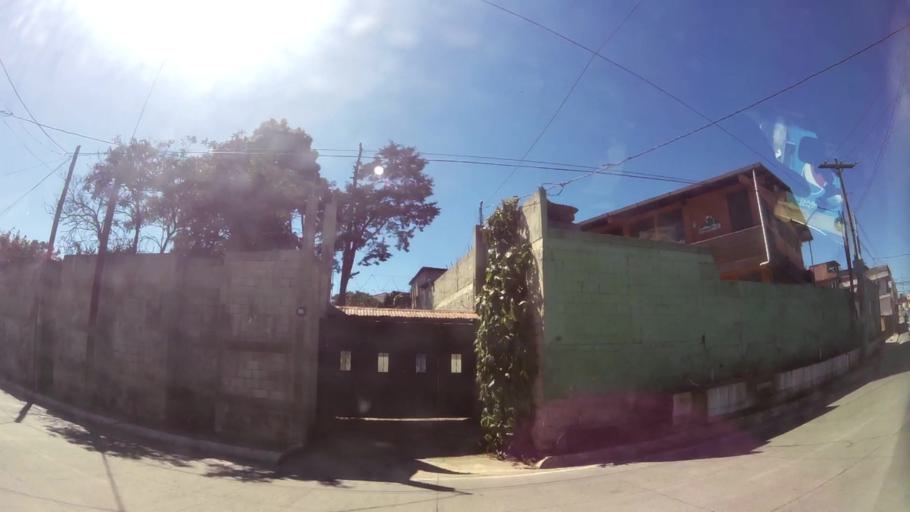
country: GT
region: Guatemala
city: San Jose Pinula
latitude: 14.5463
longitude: -90.4235
